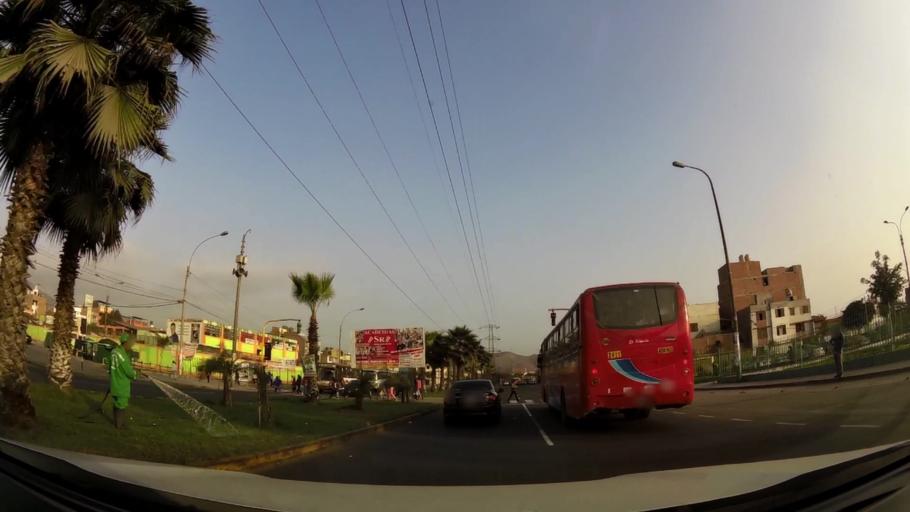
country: PE
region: Lima
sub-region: Lima
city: Independencia
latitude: -11.9817
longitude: -77.0724
